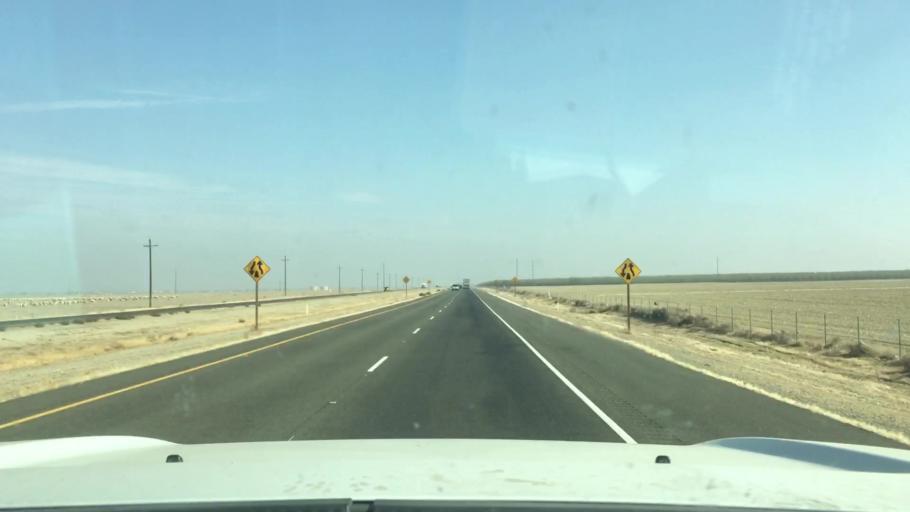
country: US
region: California
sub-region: Kern County
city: Lost Hills
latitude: 35.6157
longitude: -119.7681
